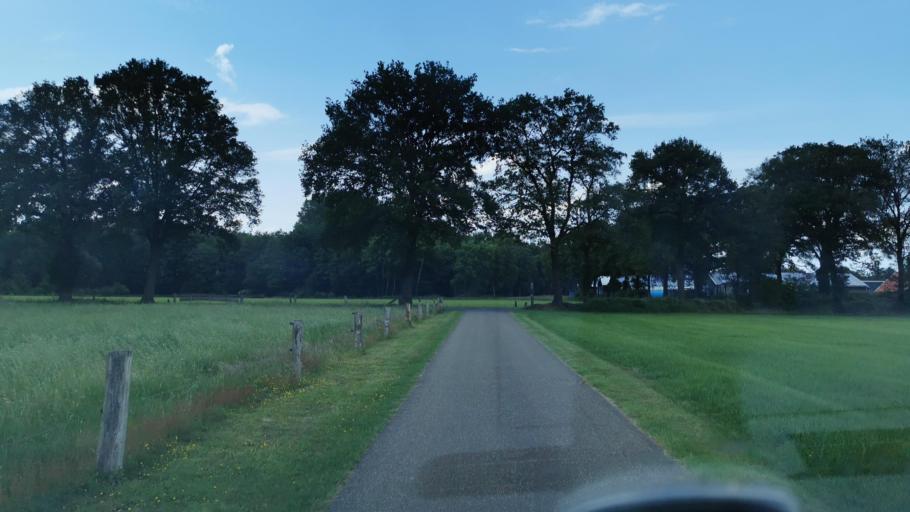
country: NL
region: Overijssel
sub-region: Gemeente Hengelo
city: Hengelo
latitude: 52.3278
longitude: 6.8360
